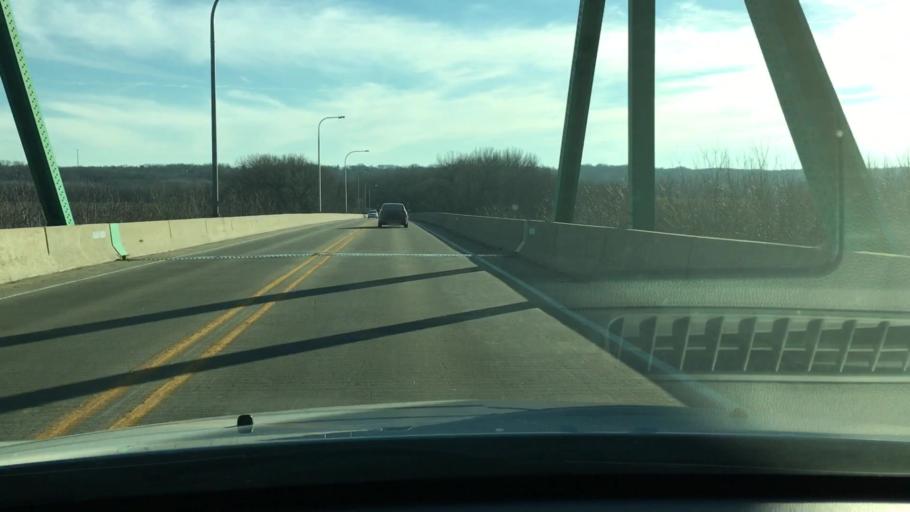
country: US
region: Illinois
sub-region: LaSalle County
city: Peru
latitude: 41.3225
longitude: -89.1199
